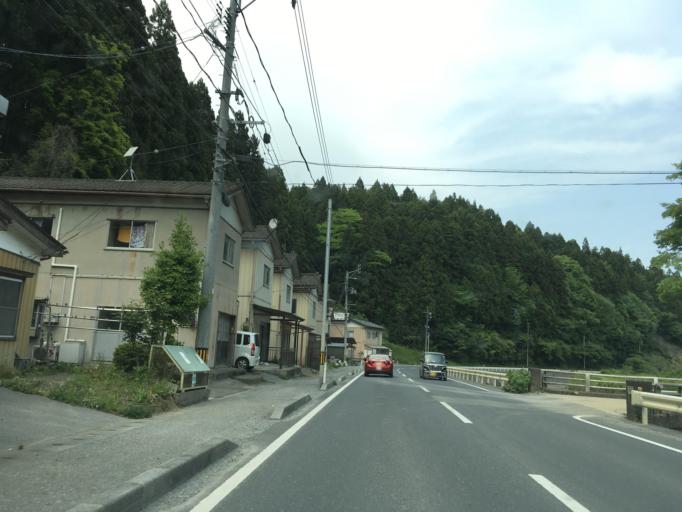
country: JP
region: Iwate
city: Ofunato
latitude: 38.8840
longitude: 141.5467
